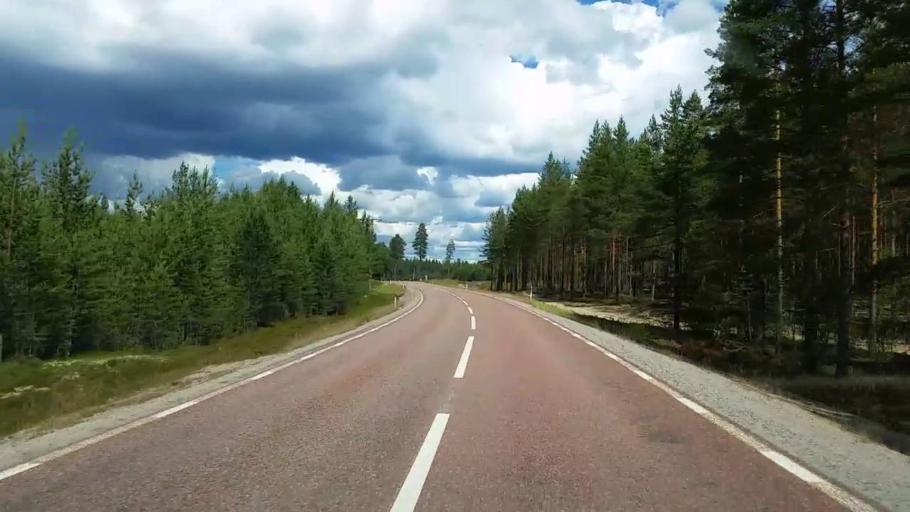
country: SE
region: Gaevleborg
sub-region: Ovanakers Kommun
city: Edsbyn
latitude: 61.3450
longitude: 15.5684
